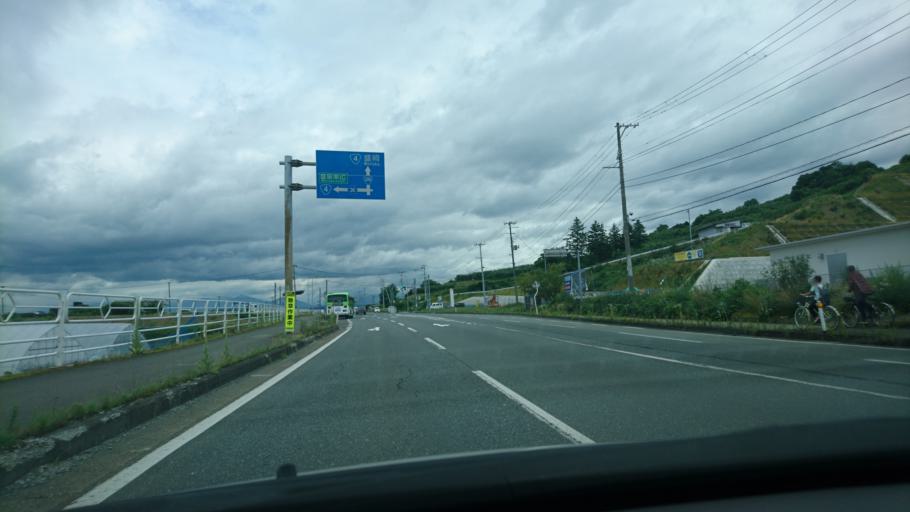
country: JP
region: Iwate
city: Morioka-shi
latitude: 39.6602
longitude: 141.1783
